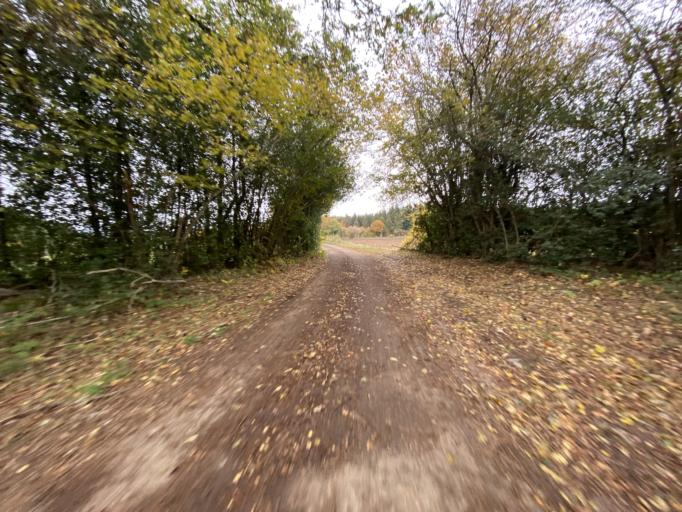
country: FR
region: Bourgogne
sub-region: Departement de la Cote-d'Or
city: Saulieu
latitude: 47.2726
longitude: 4.1619
